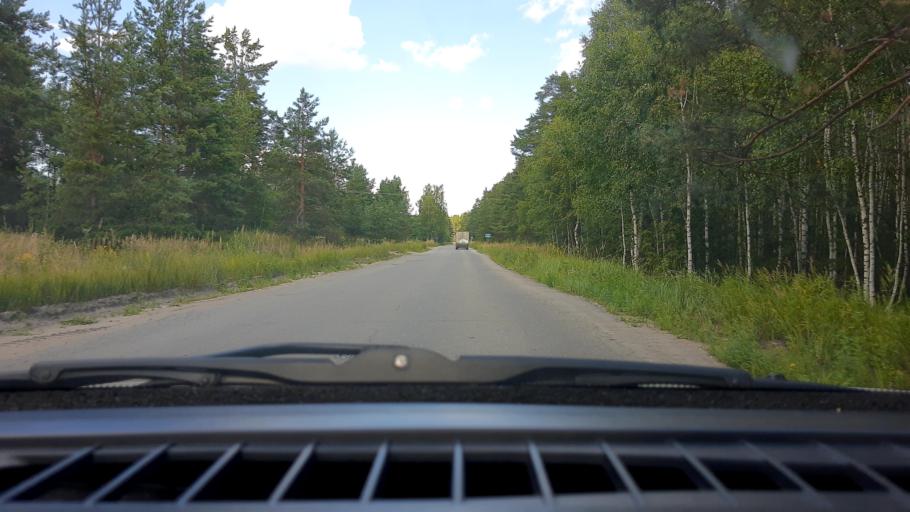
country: RU
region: Nizjnij Novgorod
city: Babino
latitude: 56.3203
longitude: 43.6291
